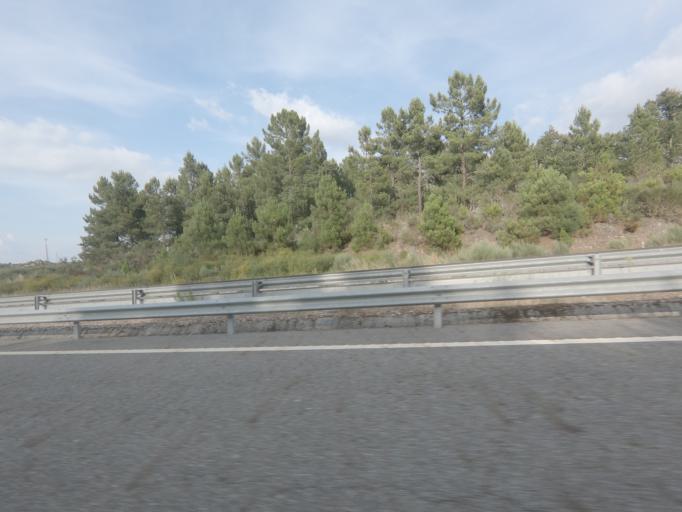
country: PT
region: Vila Real
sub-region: Chaves
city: Chaves
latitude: 41.7211
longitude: -7.5433
